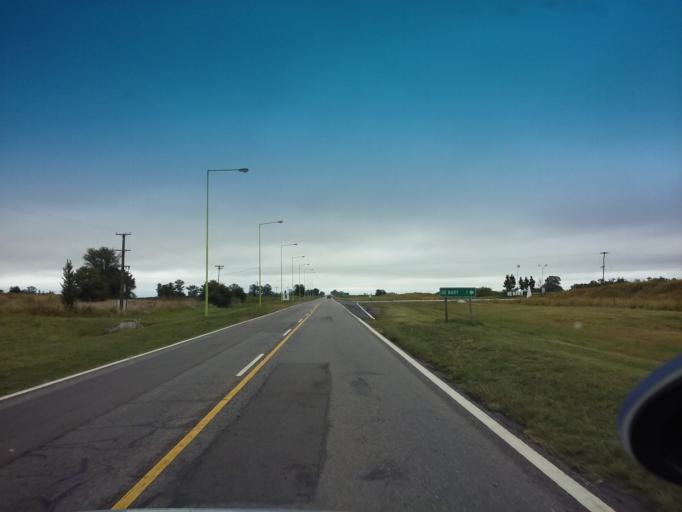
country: AR
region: Buenos Aires
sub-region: Partido de Pellegrini
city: Pellegrini
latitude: -36.3470
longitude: -63.2516
